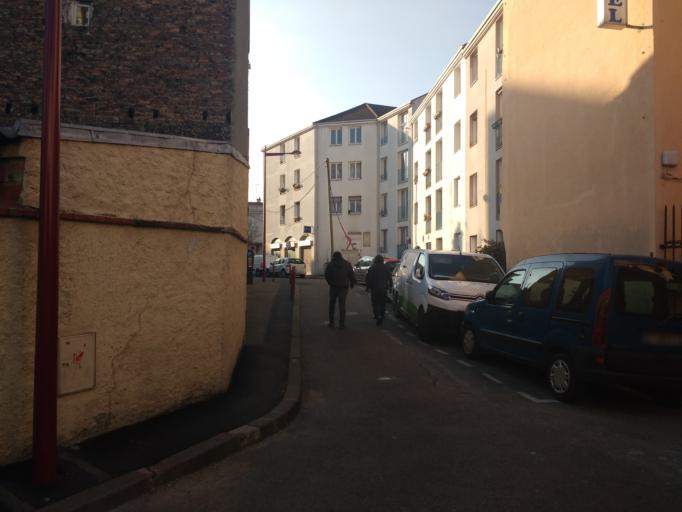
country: FR
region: Ile-de-France
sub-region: Departement de Seine-Saint-Denis
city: Le Pre-Saint-Gervais
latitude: 48.8828
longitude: 2.4038
